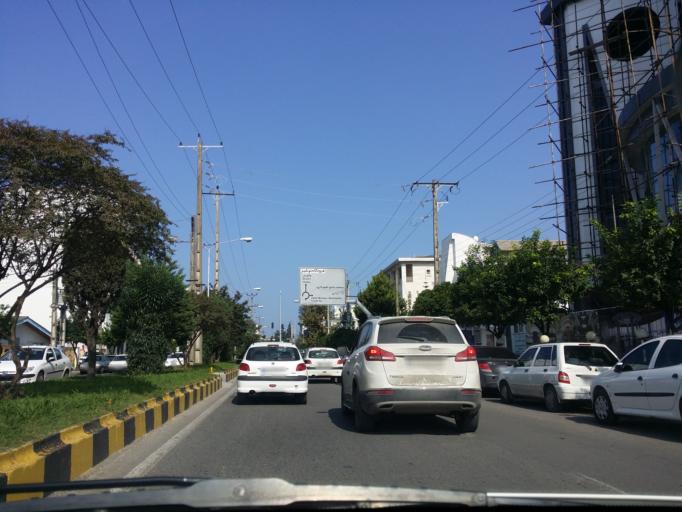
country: IR
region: Mazandaran
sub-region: Nowshahr
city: Nowshahr
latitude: 36.6515
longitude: 51.4947
